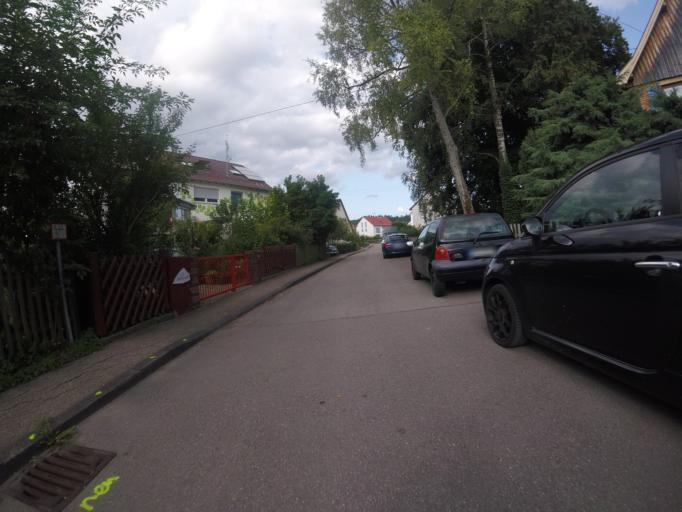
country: DE
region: Baden-Wuerttemberg
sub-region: Regierungsbezirk Stuttgart
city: Aspach
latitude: 48.9902
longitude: 9.4092
